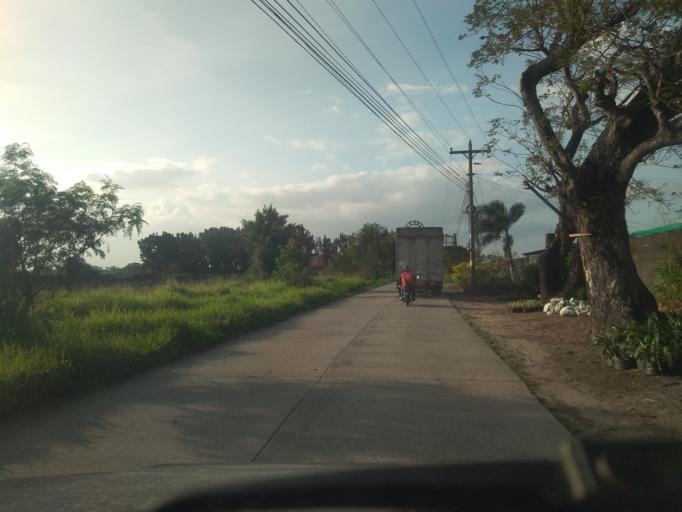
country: PH
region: Central Luzon
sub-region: Province of Pampanga
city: Malino
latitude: 15.1077
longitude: 120.6703
